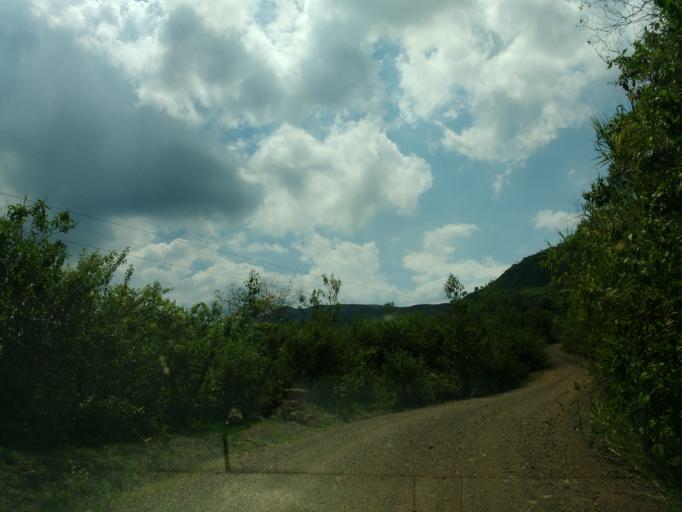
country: CO
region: Cauca
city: Buenos Aires
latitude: 3.1027
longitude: -76.6872
